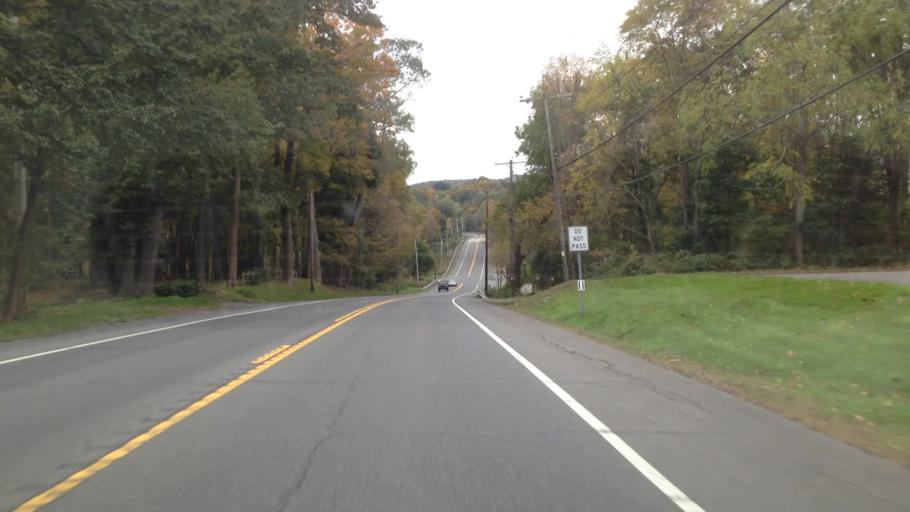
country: US
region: New York
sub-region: Dutchess County
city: Hyde Park
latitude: 41.7968
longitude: -73.9594
